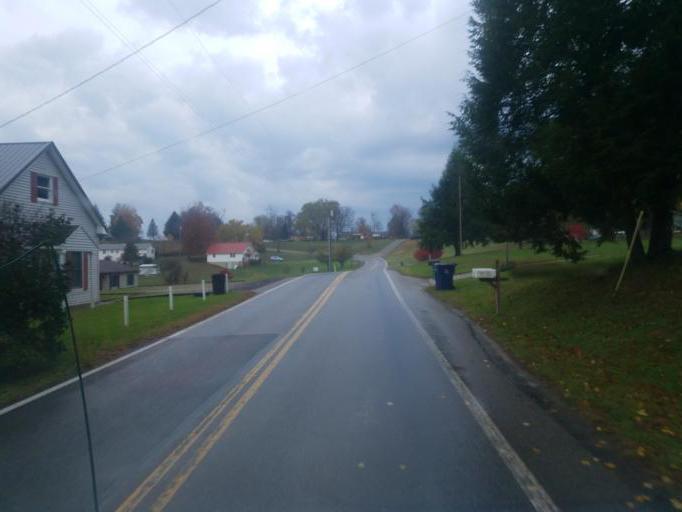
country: US
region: Ohio
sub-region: Morgan County
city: McConnelsville
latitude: 39.4913
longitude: -81.8706
